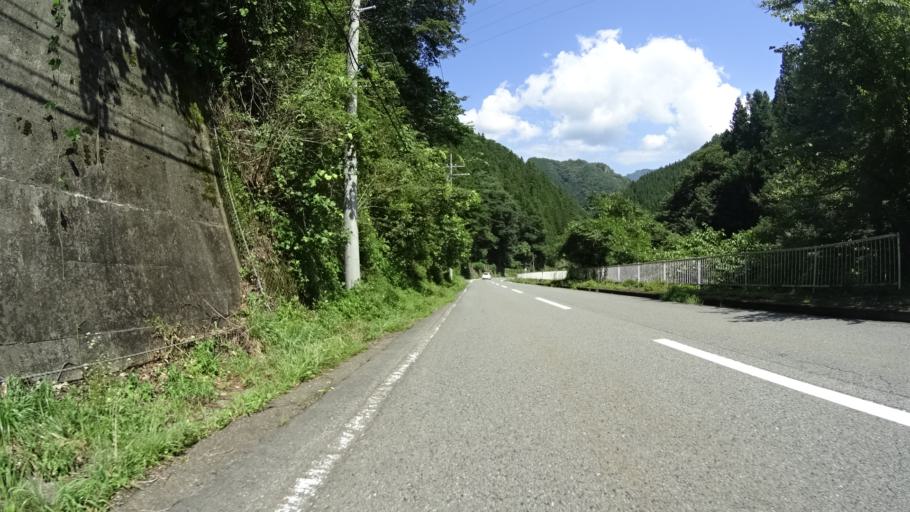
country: JP
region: Gunma
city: Tomioka
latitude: 36.0768
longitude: 138.8254
